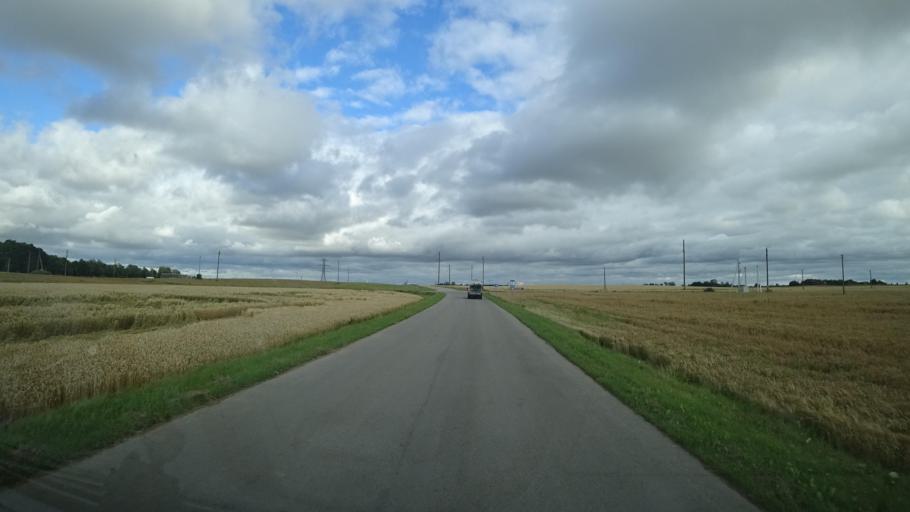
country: LT
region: Marijampoles apskritis
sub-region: Marijampole Municipality
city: Marijampole
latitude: 54.5178
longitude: 23.3256
